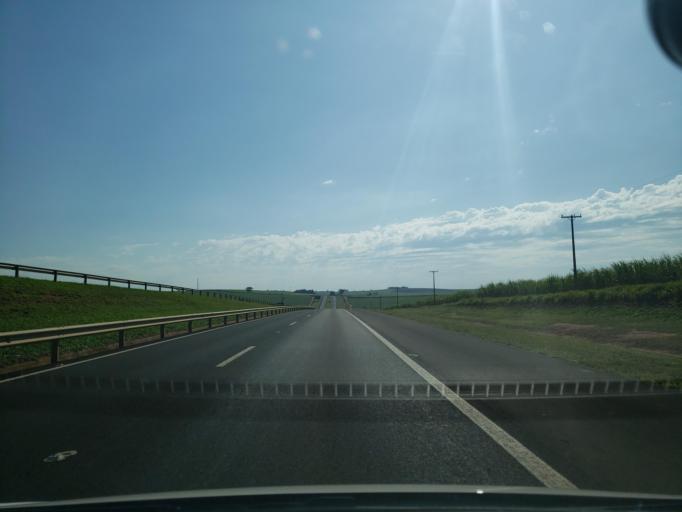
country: BR
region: Sao Paulo
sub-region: Promissao
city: Promissao
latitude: -21.5314
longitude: -49.9840
